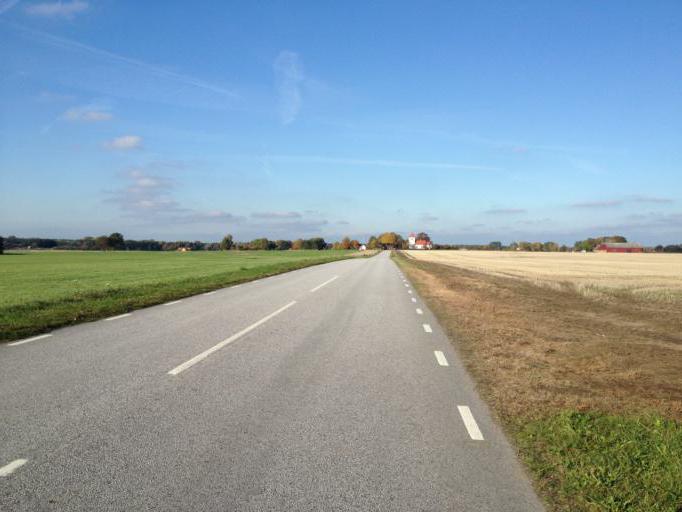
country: SE
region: Skane
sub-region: Kavlinge Kommun
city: Hofterup
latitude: 55.7786
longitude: 12.9753
